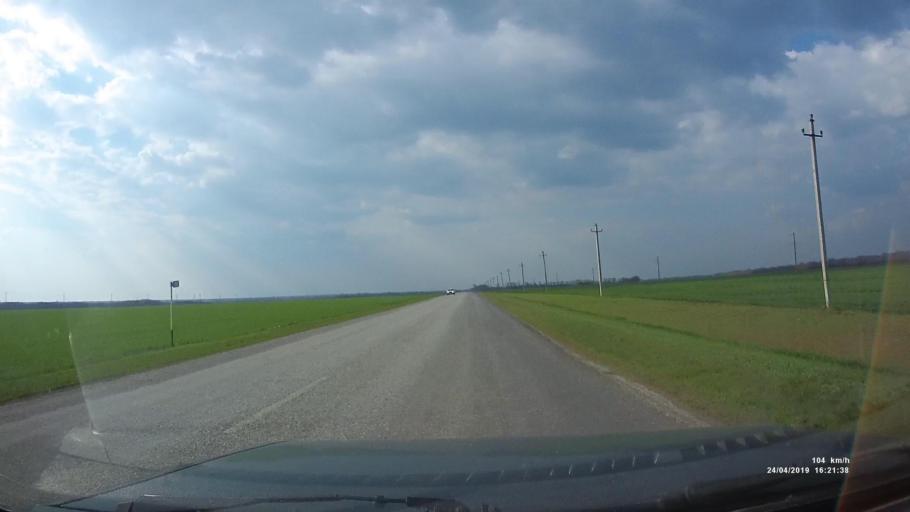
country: RU
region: Rostov
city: Orlovskiy
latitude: 46.8076
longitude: 42.0636
